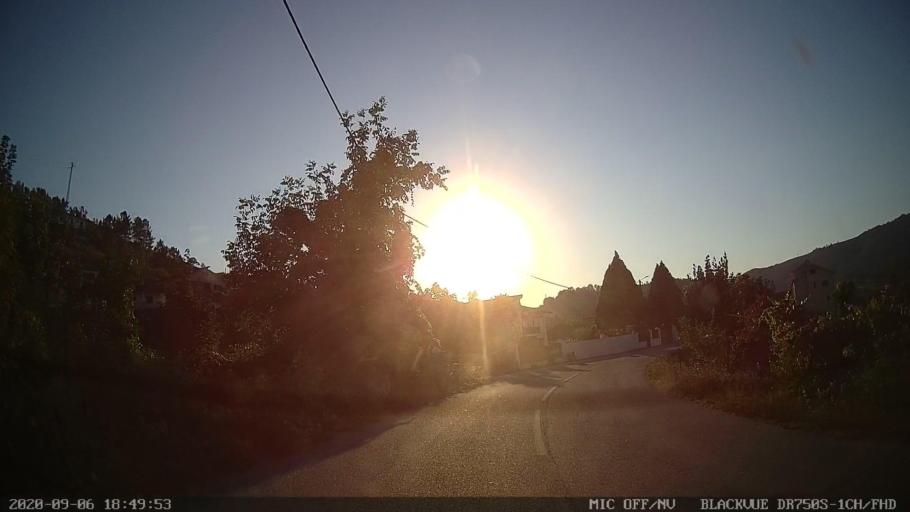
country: PT
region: Porto
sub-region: Amarante
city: Amarante
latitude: 41.2618
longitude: -7.9978
